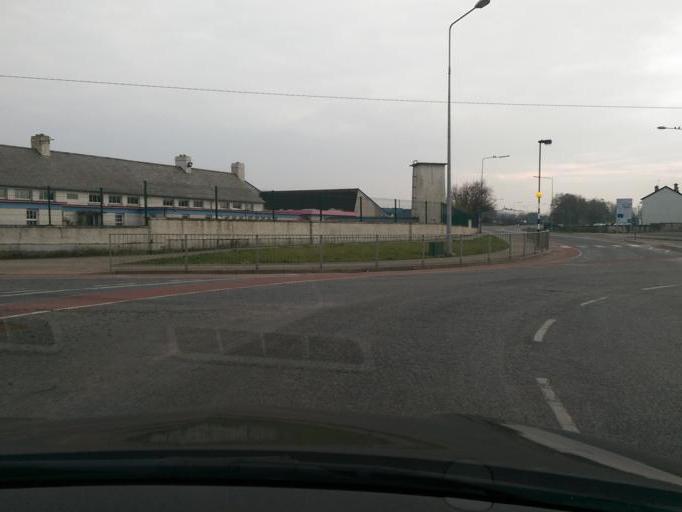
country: IE
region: Leinster
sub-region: An Iarmhi
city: Athlone
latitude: 53.4359
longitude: -7.9024
